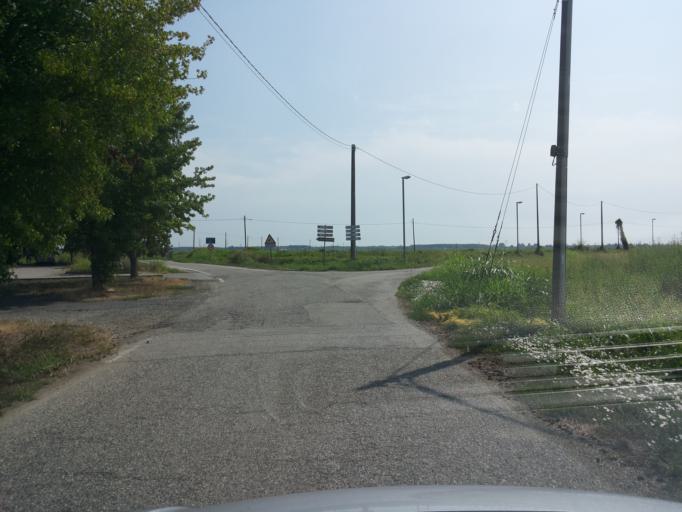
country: IT
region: Piedmont
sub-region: Provincia di Vercelli
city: Pezzana
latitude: 45.2649
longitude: 8.4969
